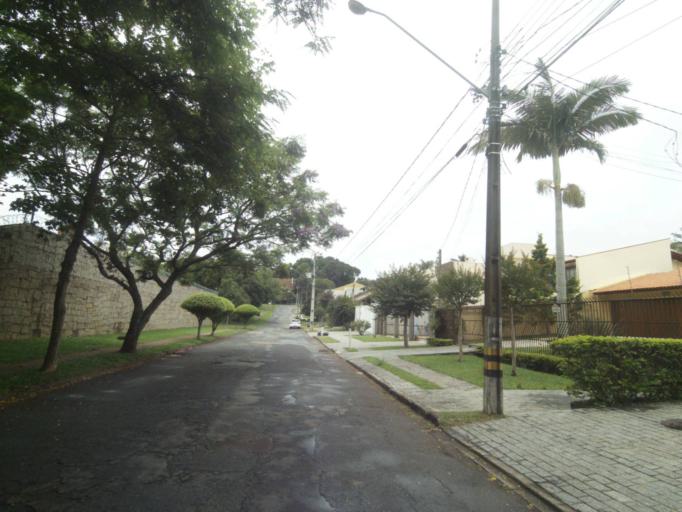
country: BR
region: Parana
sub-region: Curitiba
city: Curitiba
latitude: -25.4082
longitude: -49.2856
